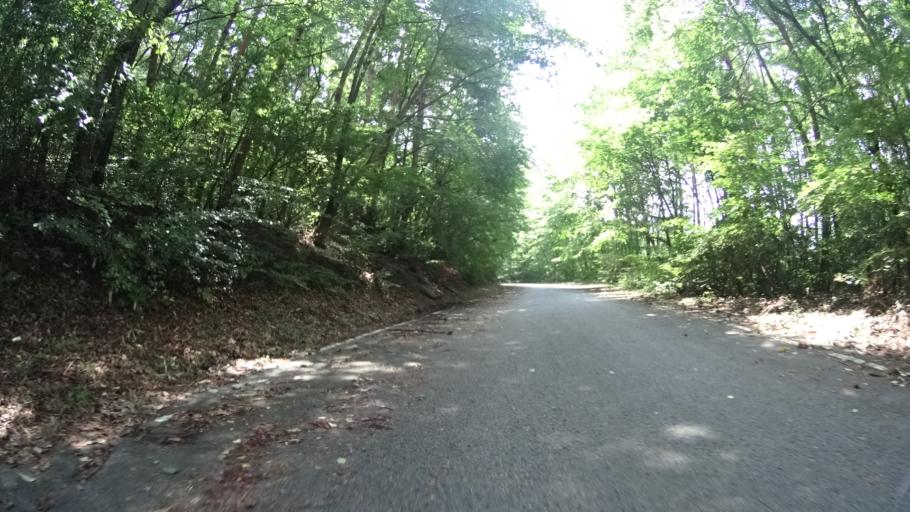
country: JP
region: Yamanashi
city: Nirasaki
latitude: 35.8878
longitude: 138.4764
